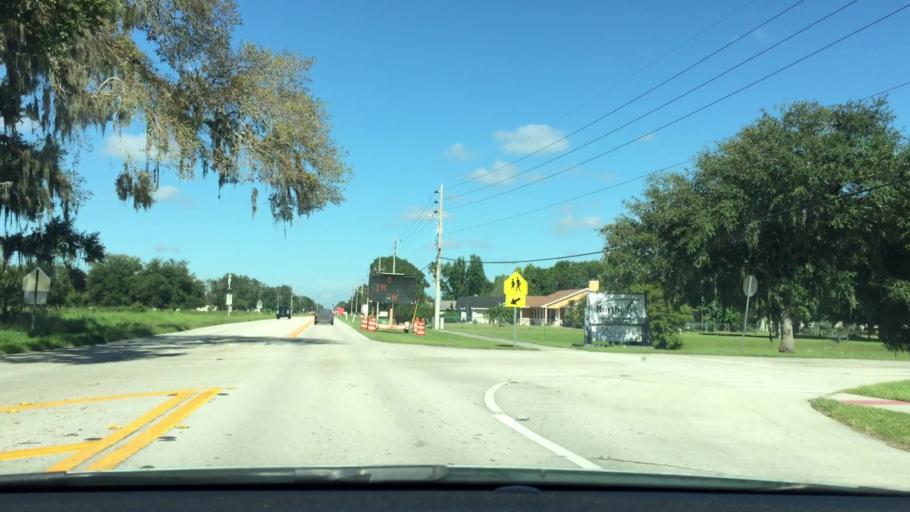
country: US
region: Florida
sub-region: Osceola County
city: Saint Cloud
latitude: 28.2789
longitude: -81.3266
